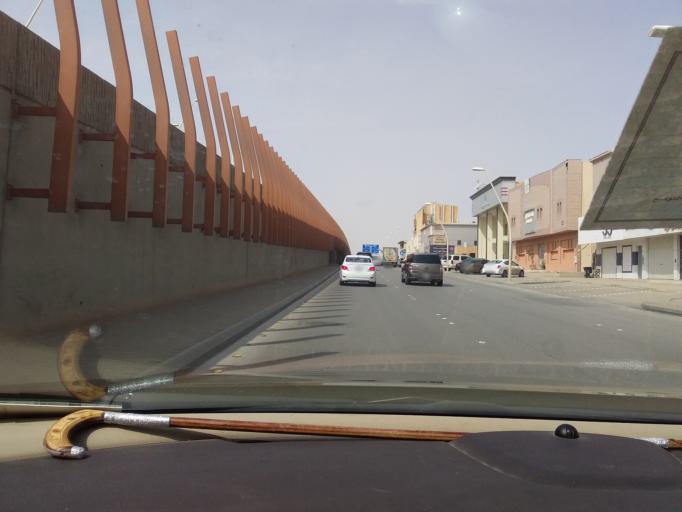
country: SA
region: Ar Riyad
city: Riyadh
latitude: 24.7414
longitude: 46.7048
